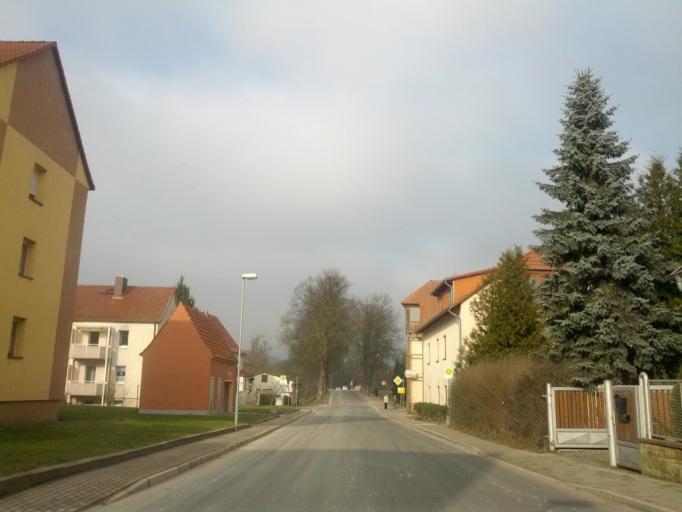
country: DE
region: Thuringia
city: Mihla
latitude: 51.0770
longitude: 10.3270
